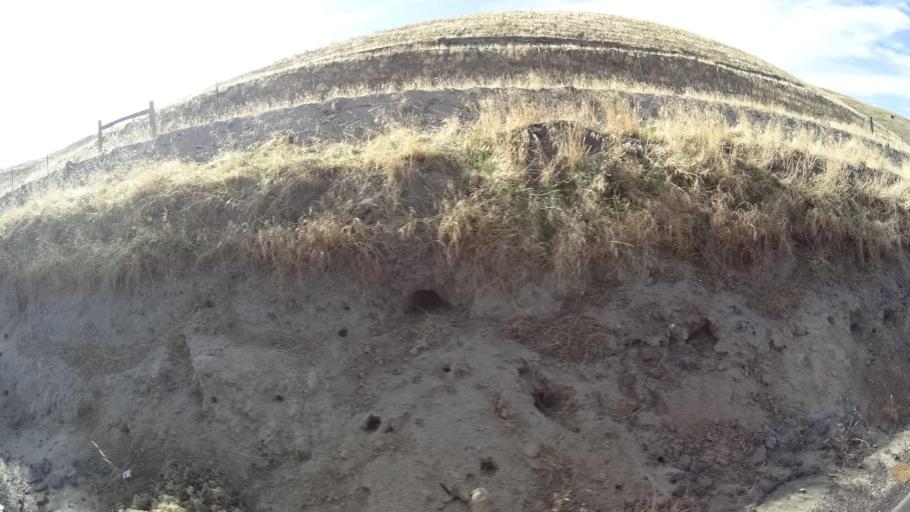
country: US
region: California
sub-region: Kern County
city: Oildale
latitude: 35.6094
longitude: -118.9075
